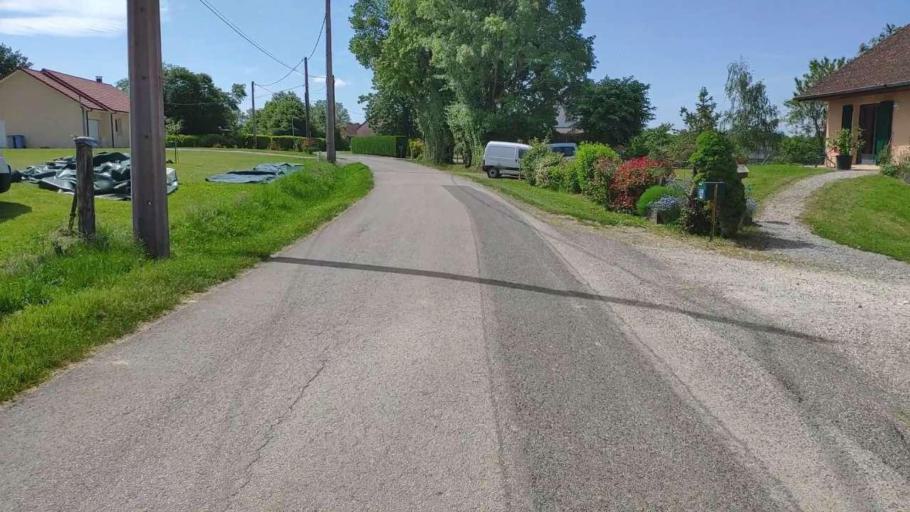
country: FR
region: Franche-Comte
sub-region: Departement du Jura
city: Bletterans
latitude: 46.7032
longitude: 5.4114
